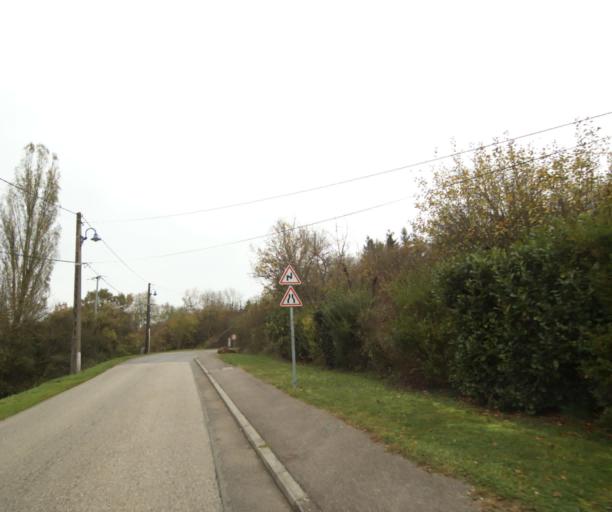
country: FR
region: Lorraine
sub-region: Departement de Meurthe-et-Moselle
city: Briey
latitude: 49.2662
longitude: 5.9143
